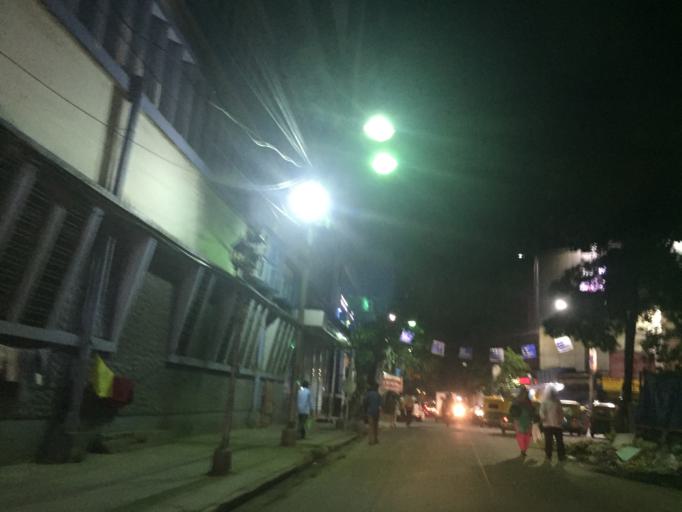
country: IN
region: West Bengal
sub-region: Kolkata
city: Bara Bazar
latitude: 22.5595
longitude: 88.3548
